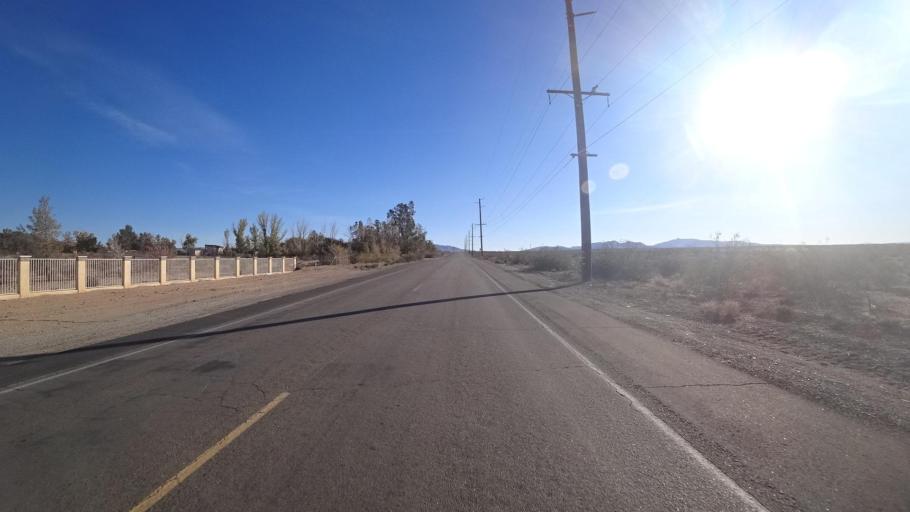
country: US
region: California
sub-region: Kern County
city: China Lake Acres
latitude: 35.6276
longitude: -117.7230
